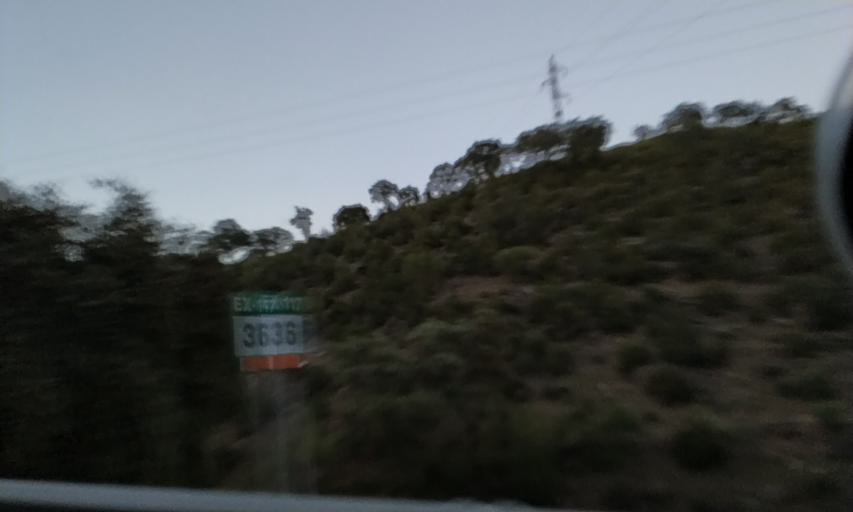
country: ES
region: Extremadura
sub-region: Provincia de Caceres
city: Alcantara
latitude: 39.7318
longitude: -6.8957
